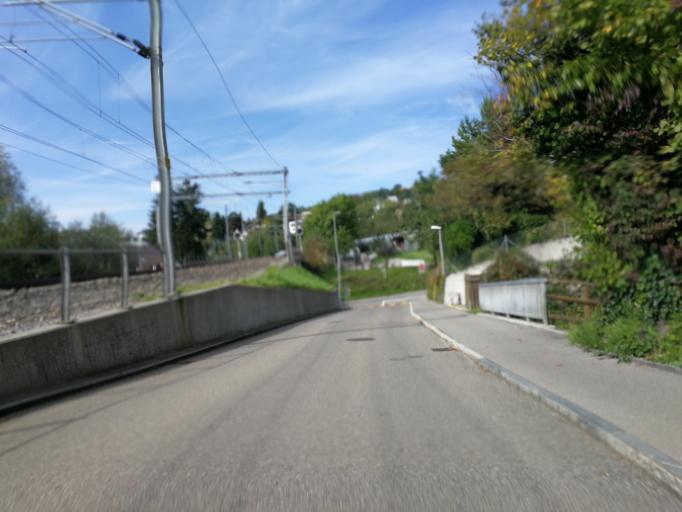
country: CH
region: Zurich
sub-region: Bezirk Meilen
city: Obermeilen
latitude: 47.2643
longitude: 8.6650
